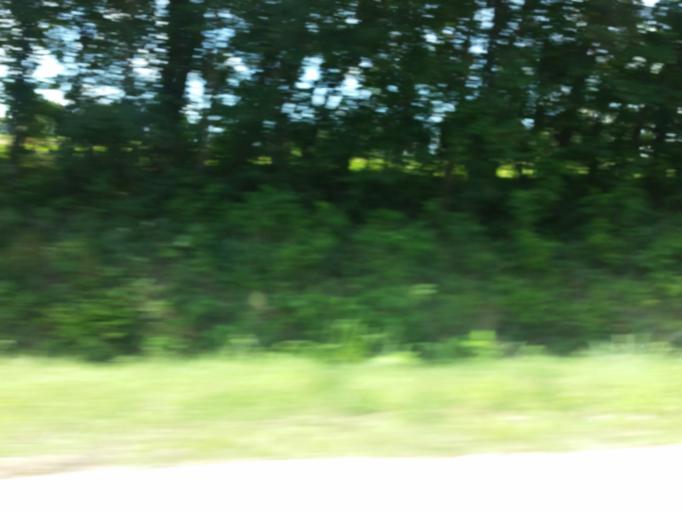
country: US
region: Tennessee
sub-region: Gibson County
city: Milan
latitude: 35.9721
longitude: -88.6940
